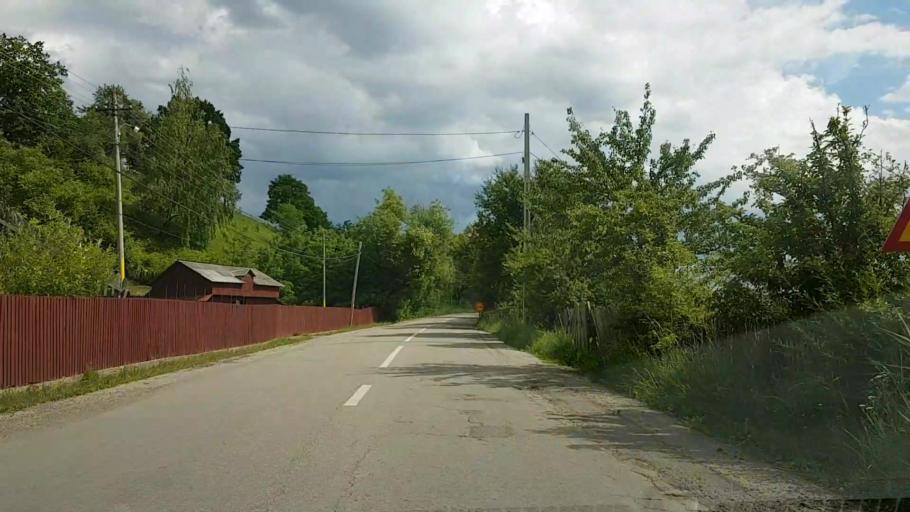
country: RO
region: Neamt
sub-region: Comuna Hangu
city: Hangu
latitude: 47.0412
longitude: 26.0565
